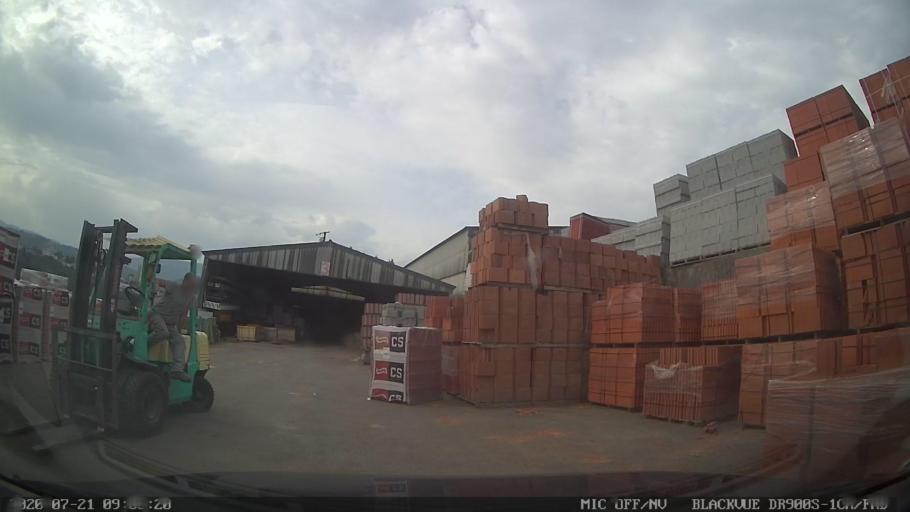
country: PT
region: Porto
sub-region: Amarante
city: Amarante
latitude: 41.2824
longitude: -8.0844
